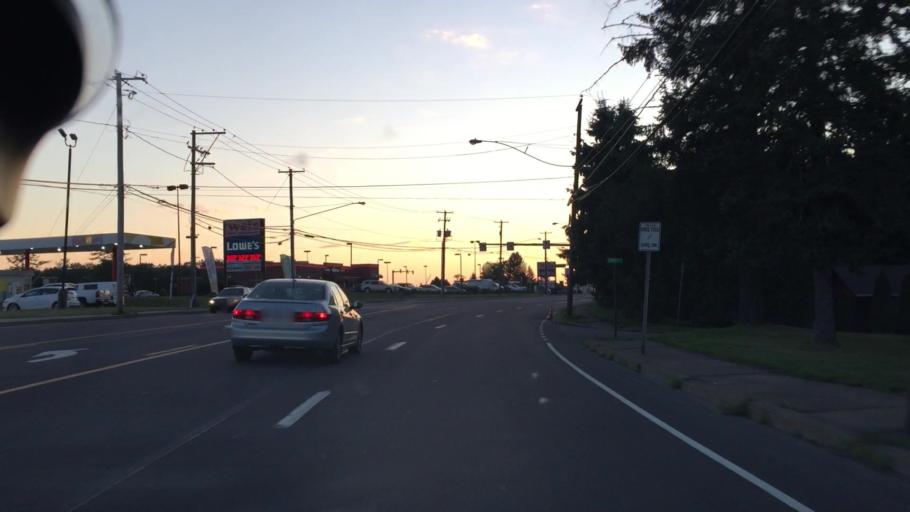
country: US
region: Pennsylvania
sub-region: Luzerne County
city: West Hazleton
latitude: 40.9672
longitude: -76.0027
